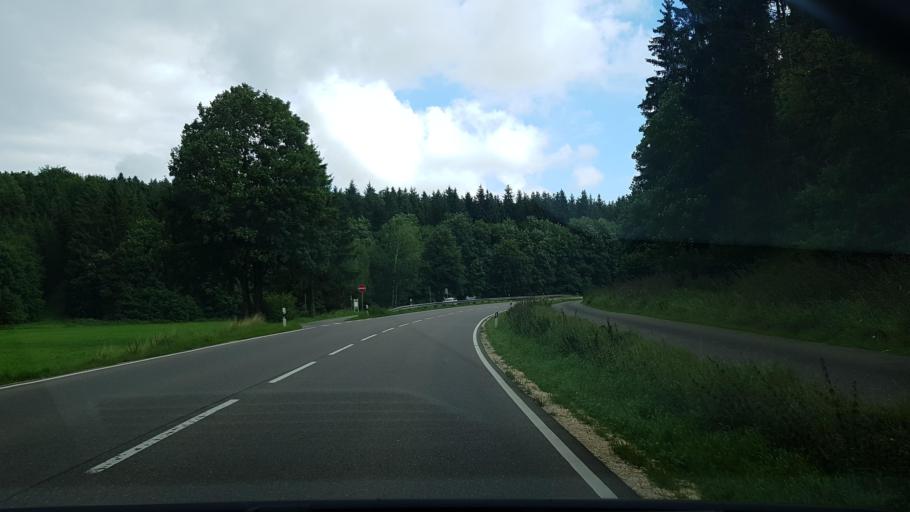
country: DE
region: Baden-Wuerttemberg
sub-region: Tuebingen Region
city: Westerheim
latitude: 48.4866
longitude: 9.5888
